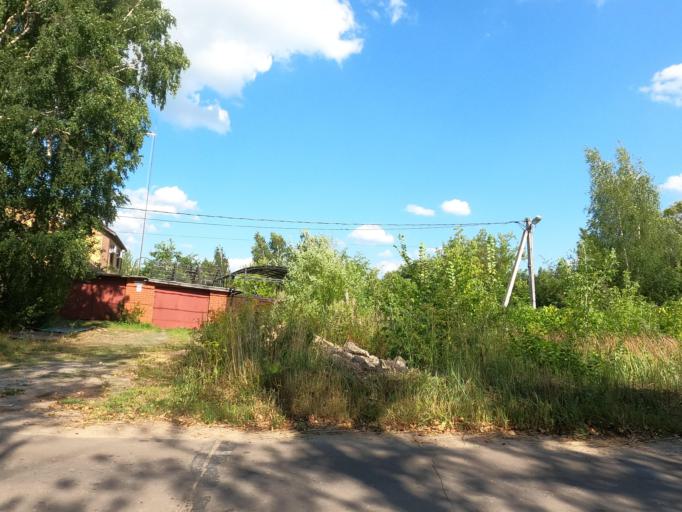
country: RU
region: Moskovskaya
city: Peski
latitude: 55.2250
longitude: 38.7519
